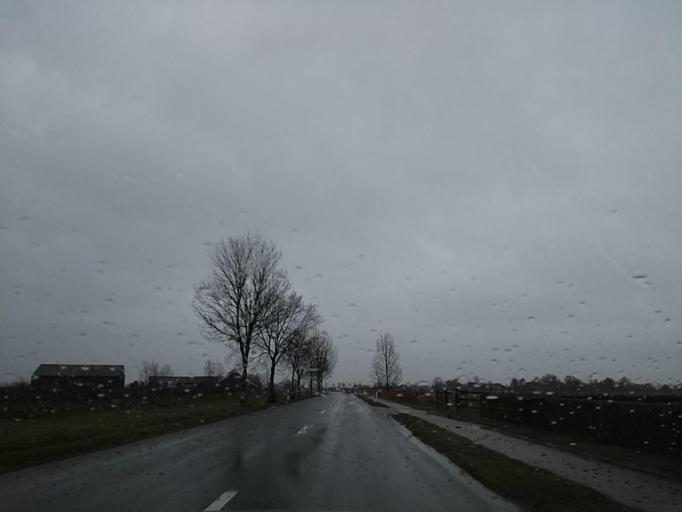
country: DE
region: Lower Saxony
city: Emden
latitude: 53.3132
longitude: 7.2871
